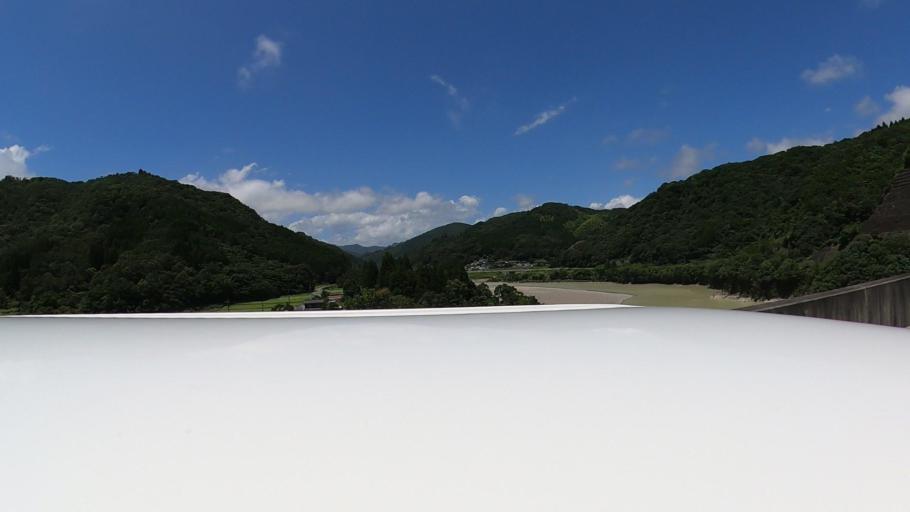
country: JP
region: Miyazaki
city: Takanabe
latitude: 32.3430
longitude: 131.5986
